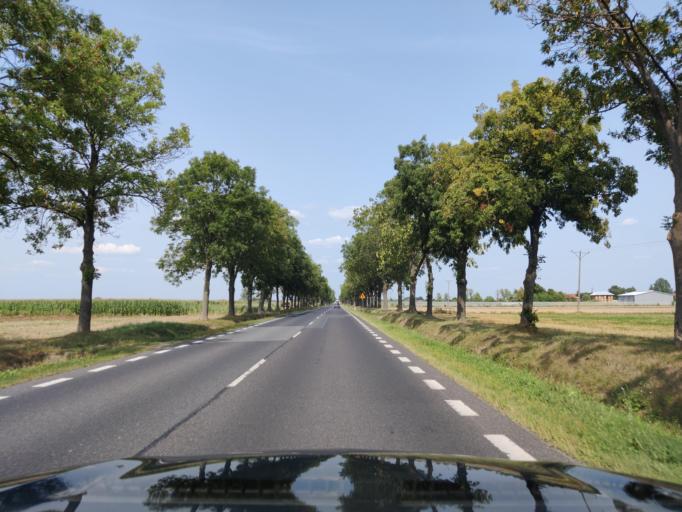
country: PL
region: Masovian Voivodeship
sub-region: Powiat pultuski
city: Pultusk
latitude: 52.7576
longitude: 21.1088
